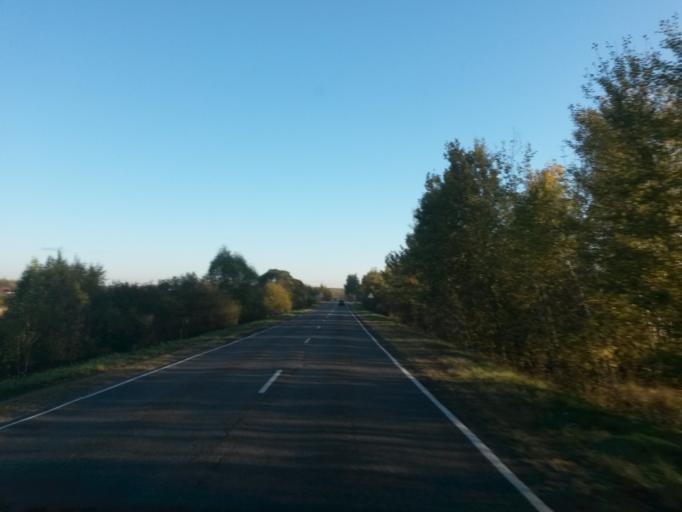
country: RU
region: Moskovskaya
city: Belyye Stolby
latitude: 55.2795
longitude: 37.7728
